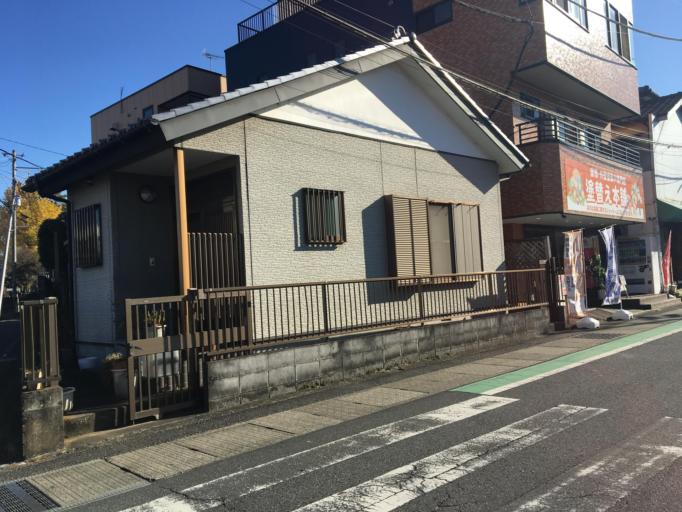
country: JP
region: Saitama
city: Satte
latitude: 36.0757
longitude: 139.7157
